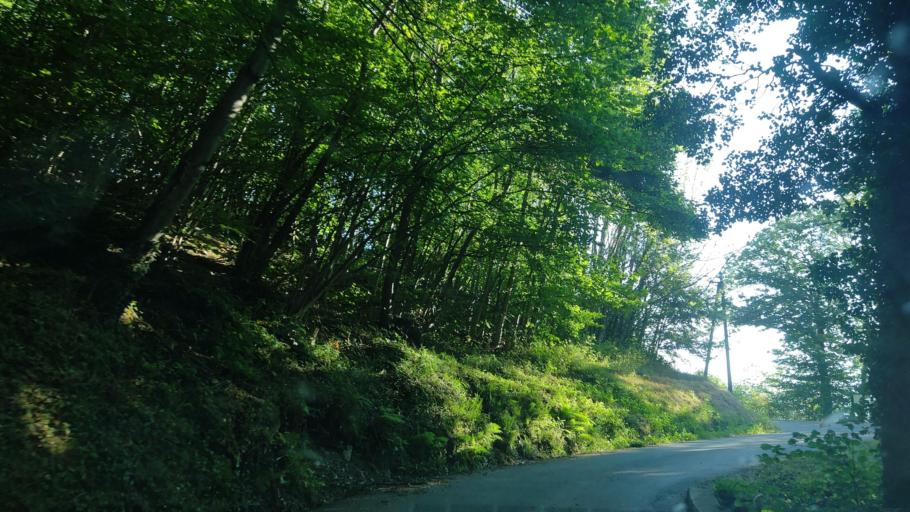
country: FR
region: Rhone-Alpes
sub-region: Departement de la Savoie
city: Saint-Etienne-de-Cuines
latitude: 45.3436
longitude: 6.2809
